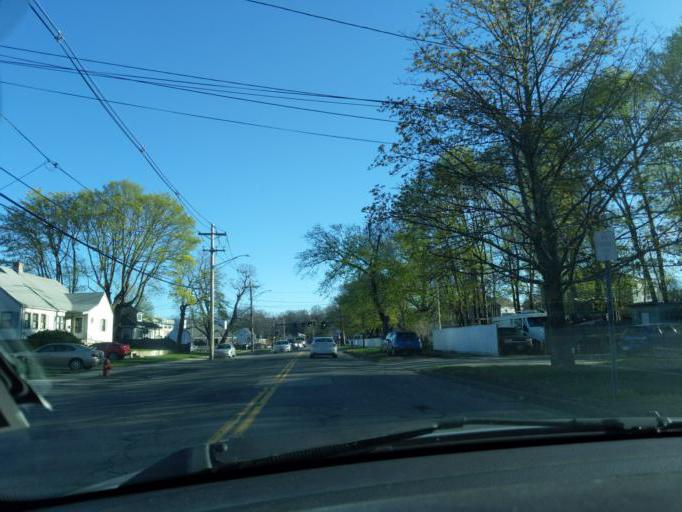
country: US
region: Massachusetts
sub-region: Essex County
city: Beverly
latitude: 42.5620
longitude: -70.8794
